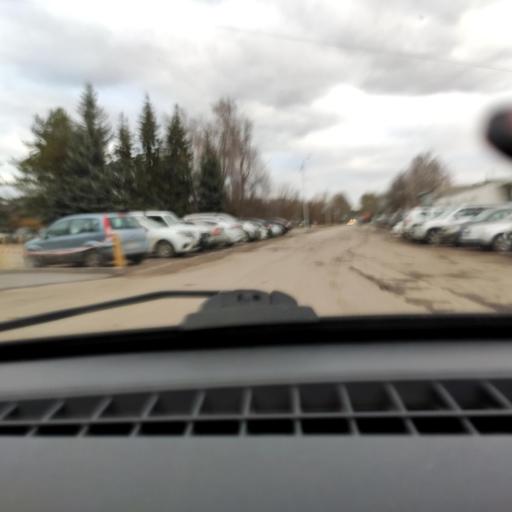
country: RU
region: Bashkortostan
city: Ufa
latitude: 54.8041
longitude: 56.0735
